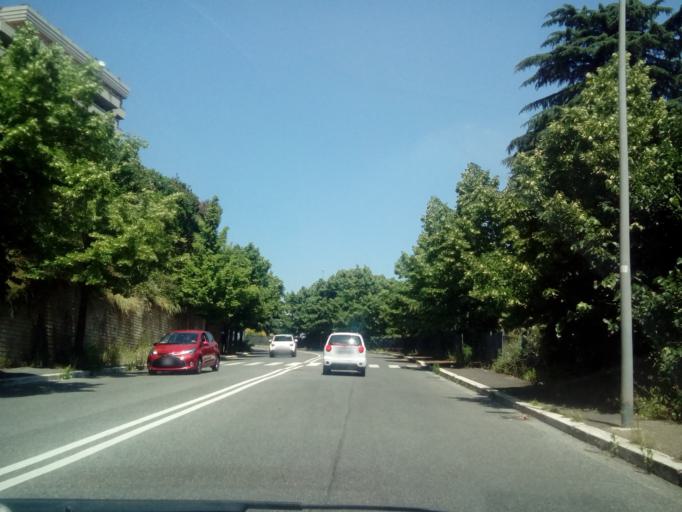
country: IT
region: Latium
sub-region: Citta metropolitana di Roma Capitale
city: Vitinia
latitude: 41.8125
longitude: 12.4502
